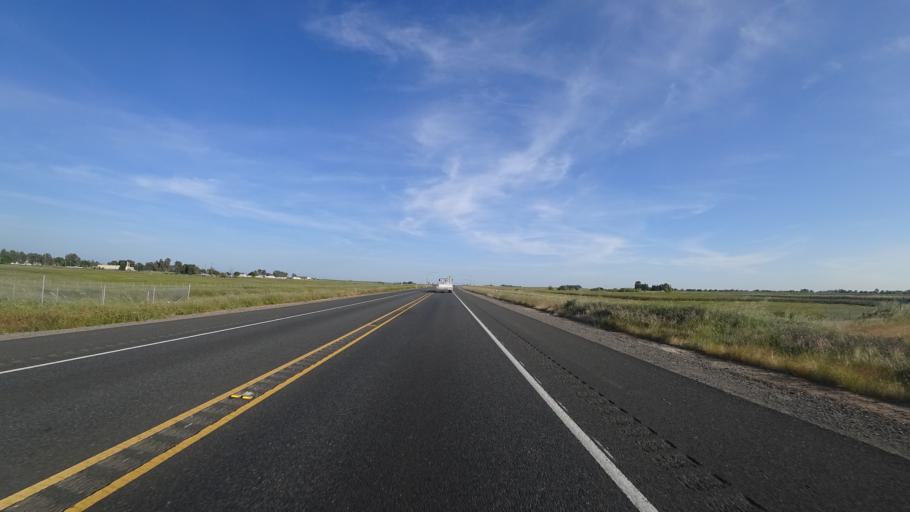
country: US
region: California
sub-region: Placer County
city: Sheridan
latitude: 38.9852
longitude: -121.3853
